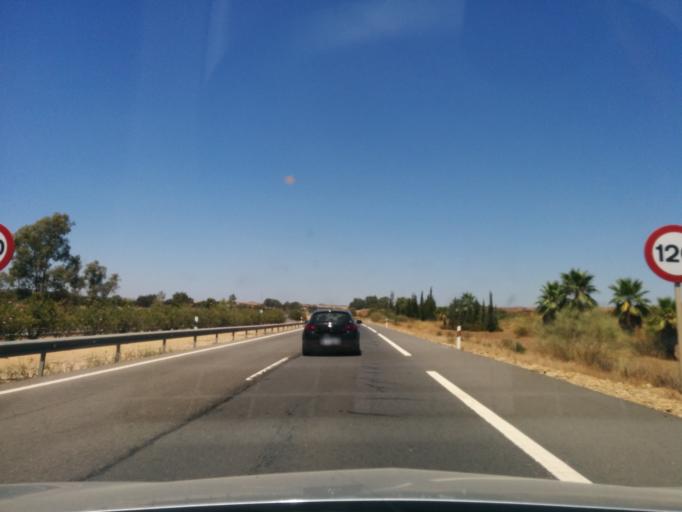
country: ES
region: Andalusia
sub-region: Provincia de Huelva
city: Gibraleon
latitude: 37.3432
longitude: -6.9223
